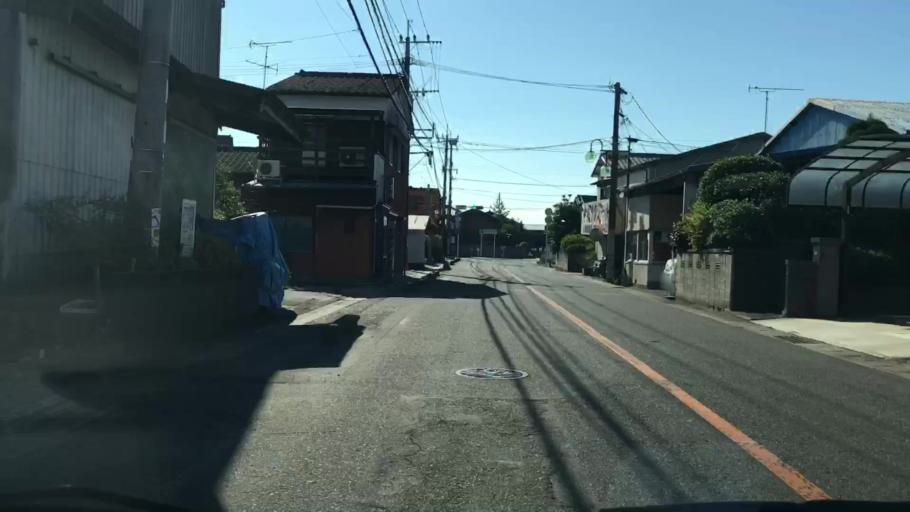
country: JP
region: Saga Prefecture
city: Okawa
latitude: 33.1895
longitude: 130.3205
